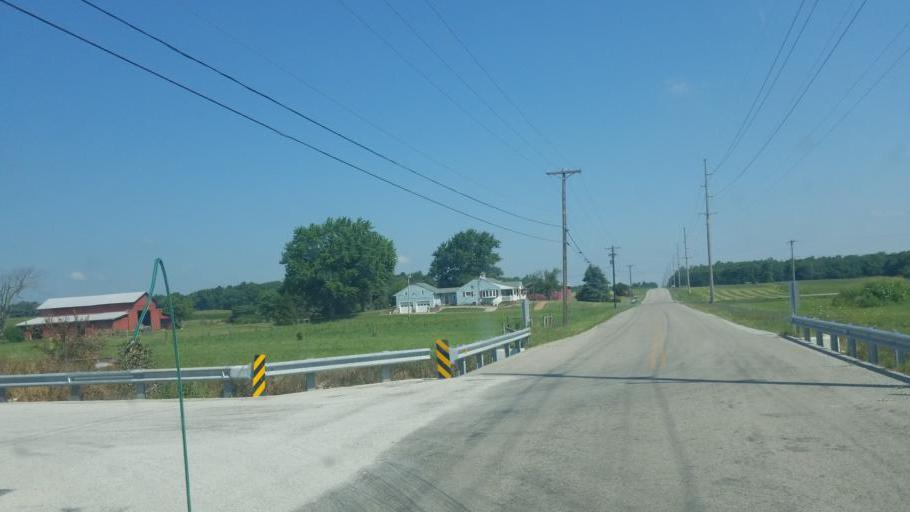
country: US
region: Ohio
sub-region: Hardin County
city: Kenton
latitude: 40.7030
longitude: -83.6536
